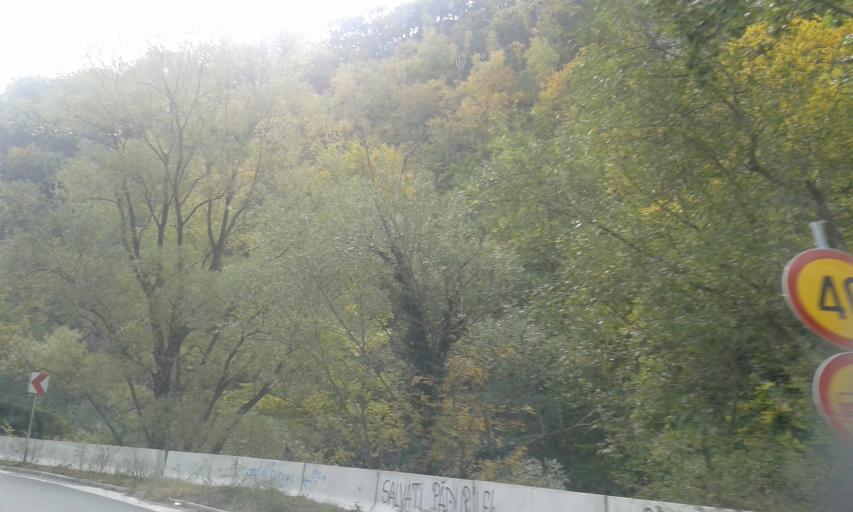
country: RO
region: Gorj
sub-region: Comuna Bumbesti-Jiu
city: Bumbesti-Jiu
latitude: 45.2053
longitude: 23.3739
